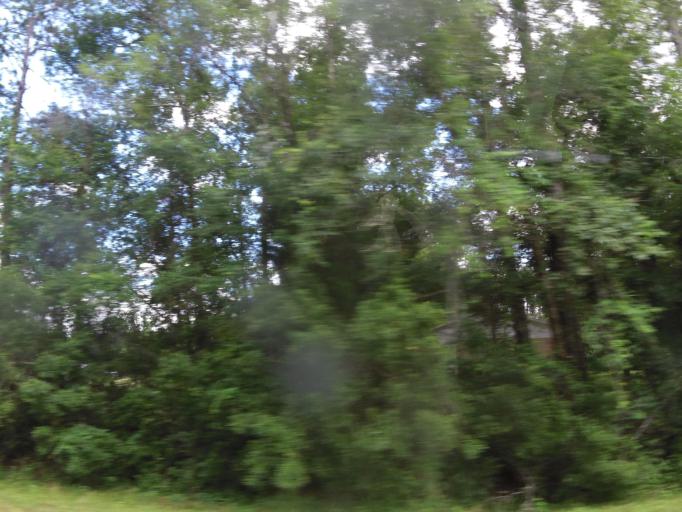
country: US
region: Florida
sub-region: Clay County
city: Green Cove Springs
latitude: 29.9189
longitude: -81.7664
